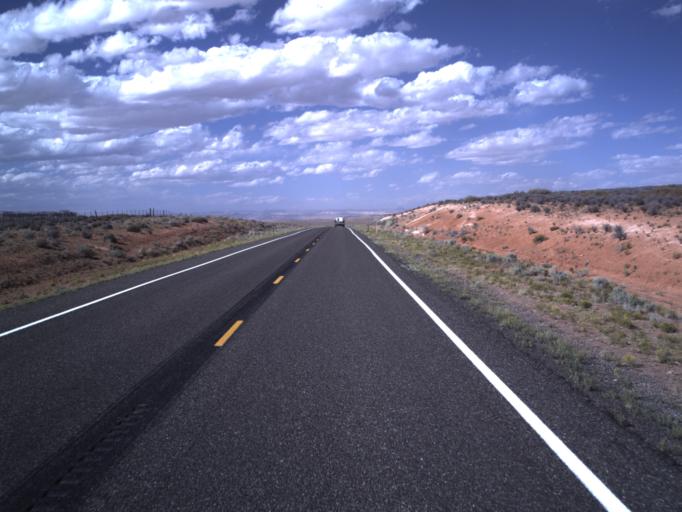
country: US
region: Utah
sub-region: Wayne County
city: Loa
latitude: 38.1614
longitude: -110.6222
